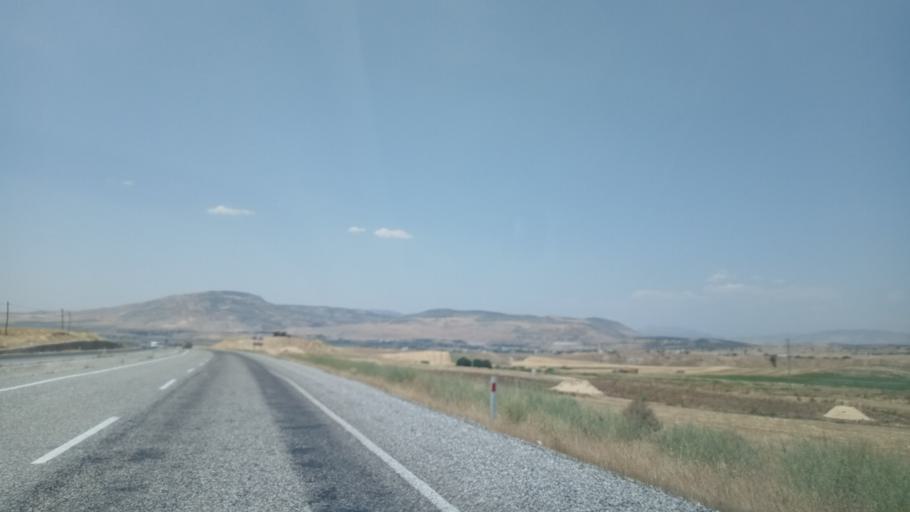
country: TR
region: Batman
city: Bekirhan
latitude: 38.1355
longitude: 41.2576
